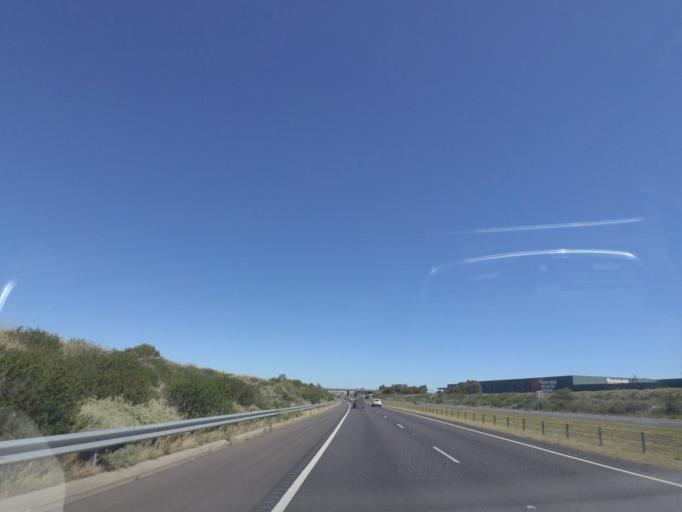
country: AU
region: Victoria
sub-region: Hume
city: Craigieburn
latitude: -37.5800
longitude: 144.9427
